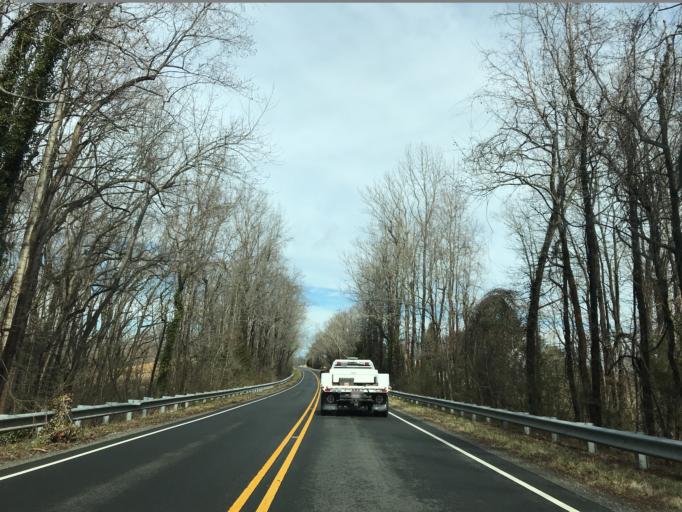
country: US
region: Virginia
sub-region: King George County
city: Dahlgren
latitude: 38.3216
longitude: -77.0804
